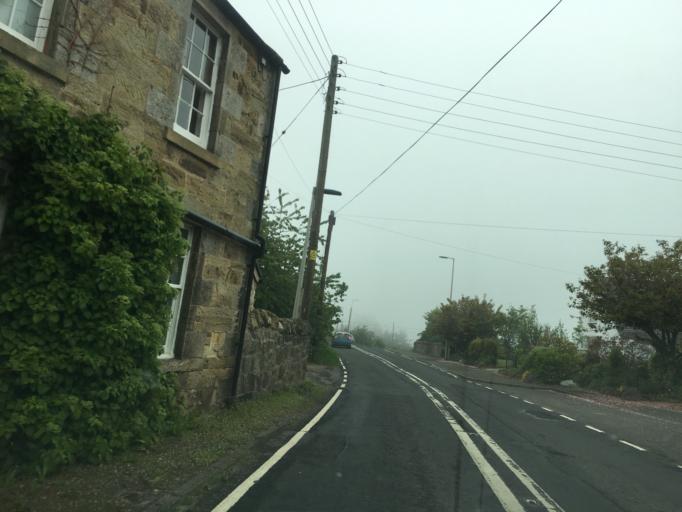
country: GB
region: Scotland
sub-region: Midlothian
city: Penicuik
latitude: 55.8292
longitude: -3.2017
